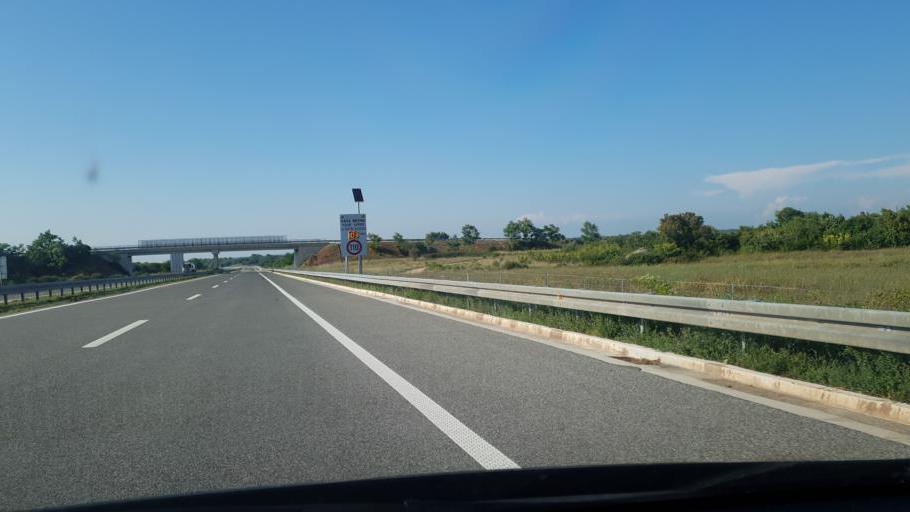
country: HR
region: Istarska
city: Vodnjan
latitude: 44.9613
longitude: 13.8724
